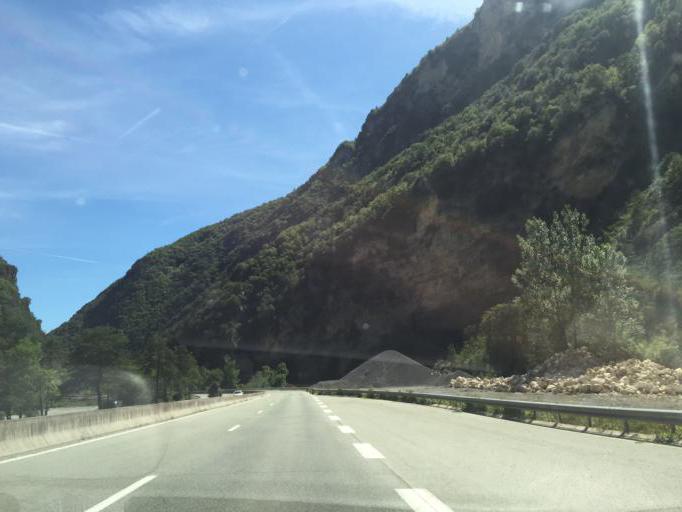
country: FR
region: Provence-Alpes-Cote d'Azur
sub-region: Departement des Alpes-Maritimes
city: Saint-Martin-Vesubie
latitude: 44.0170
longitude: 7.1311
